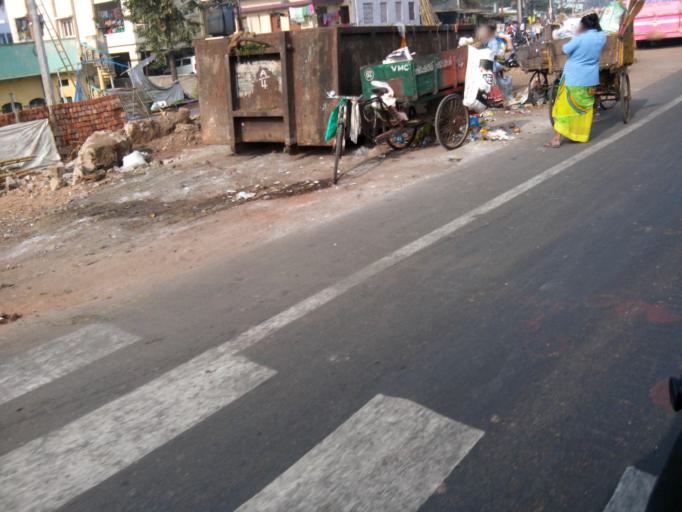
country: IN
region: Andhra Pradesh
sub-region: Krishna
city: Vijayawada
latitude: 16.5085
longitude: 80.6229
